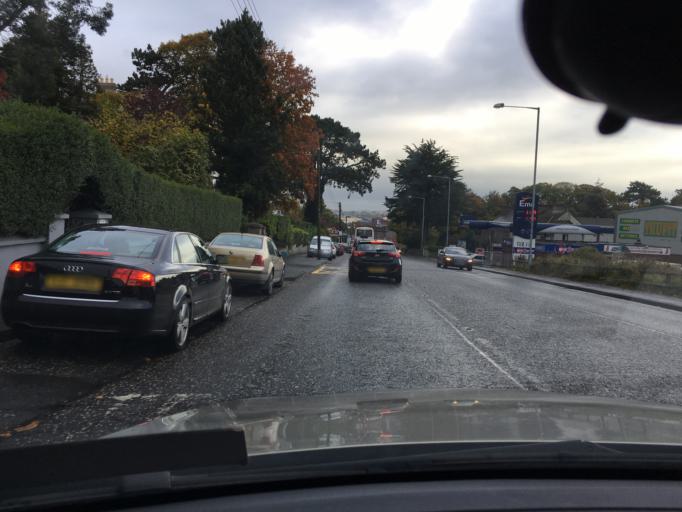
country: GB
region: Northern Ireland
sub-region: Newry and Mourne District
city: Newry
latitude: 54.1663
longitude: -6.3440
